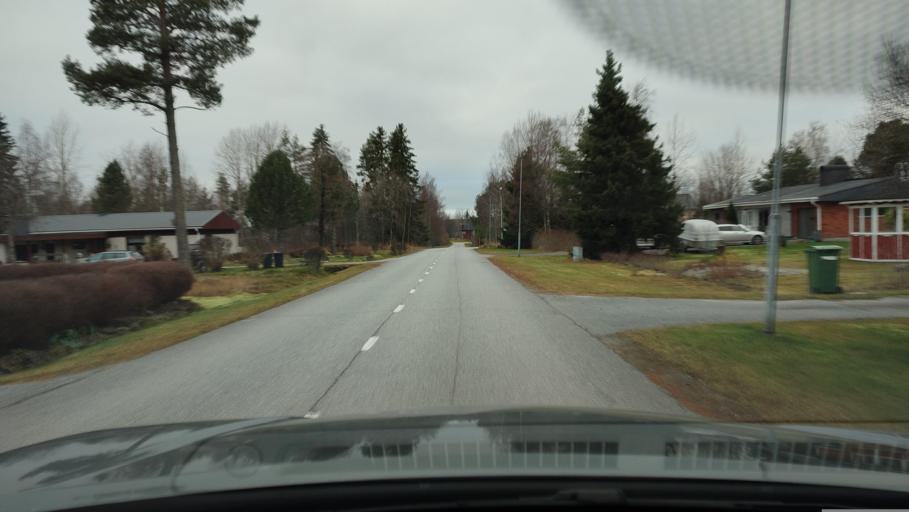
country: FI
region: Ostrobothnia
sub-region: Sydosterbotten
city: Kristinestad
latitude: 62.2666
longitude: 21.3948
